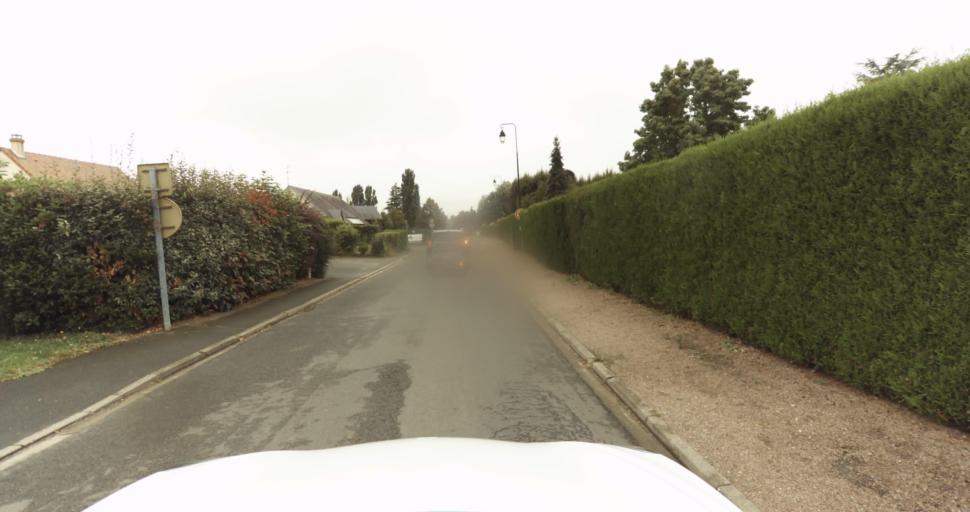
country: FR
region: Haute-Normandie
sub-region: Departement de l'Eure
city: Aviron
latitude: 49.0819
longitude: 1.0749
